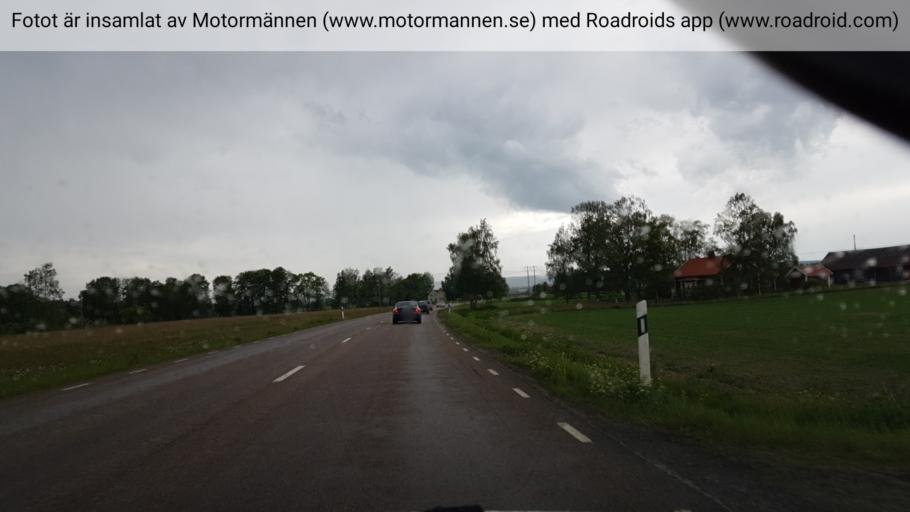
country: SE
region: Vaestra Goetaland
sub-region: Skovde Kommun
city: Skoevde
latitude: 58.3824
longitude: 13.9548
